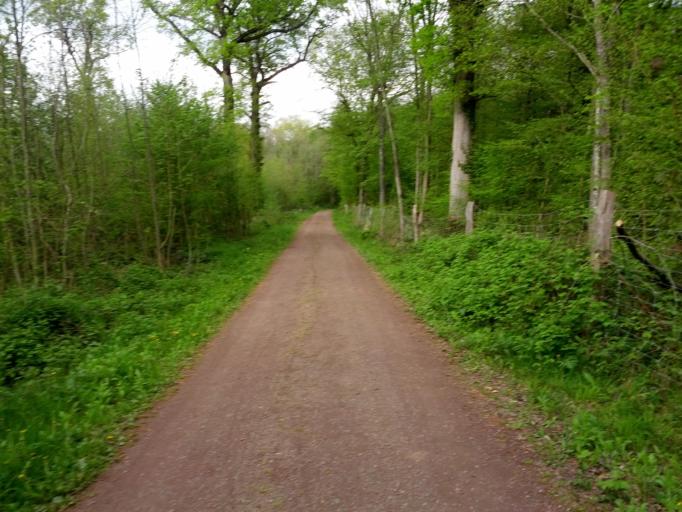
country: DE
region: Baden-Wuerttemberg
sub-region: Freiburg Region
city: Umkirch
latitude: 48.0105
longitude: 7.7566
